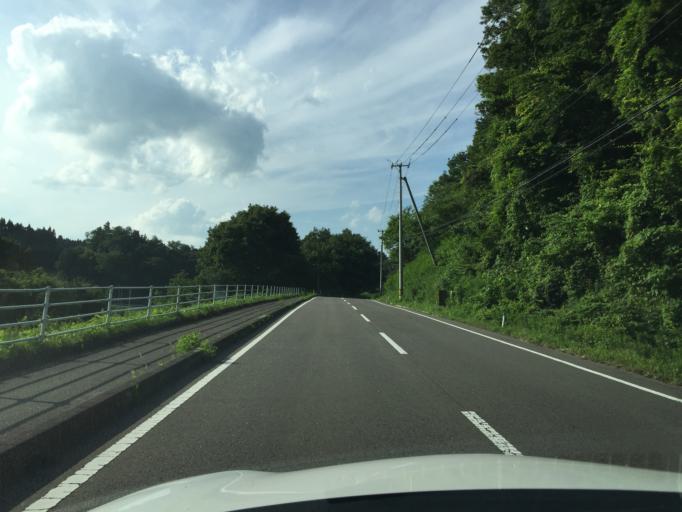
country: JP
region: Fukushima
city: Miharu
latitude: 37.4126
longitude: 140.4990
